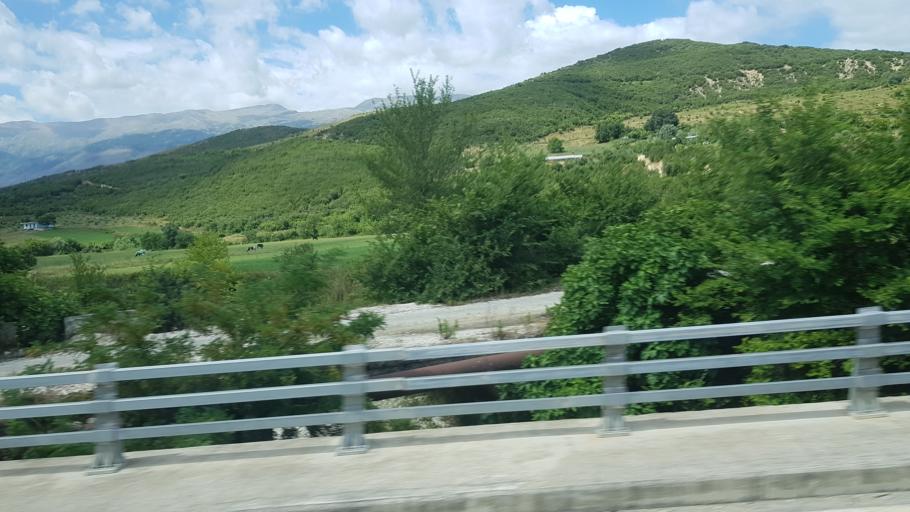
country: AL
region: Gjirokaster
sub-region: Rrethi i Tepelenes
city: Krahes
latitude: 40.4144
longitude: 19.8592
